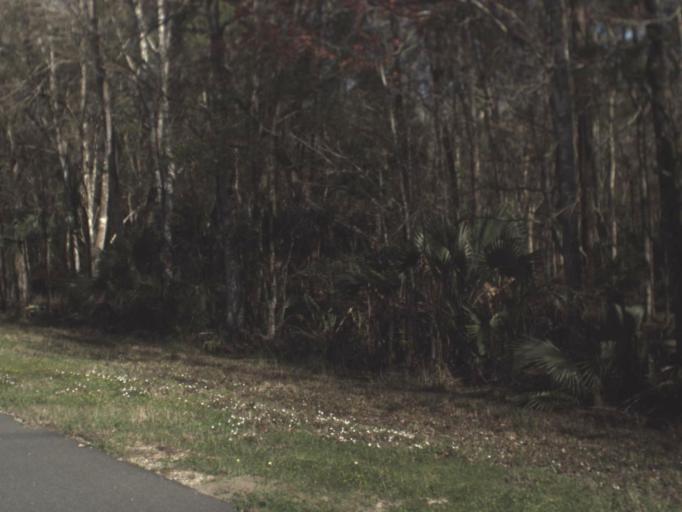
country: US
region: Florida
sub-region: Leon County
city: Woodville
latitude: 30.1576
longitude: -83.9976
